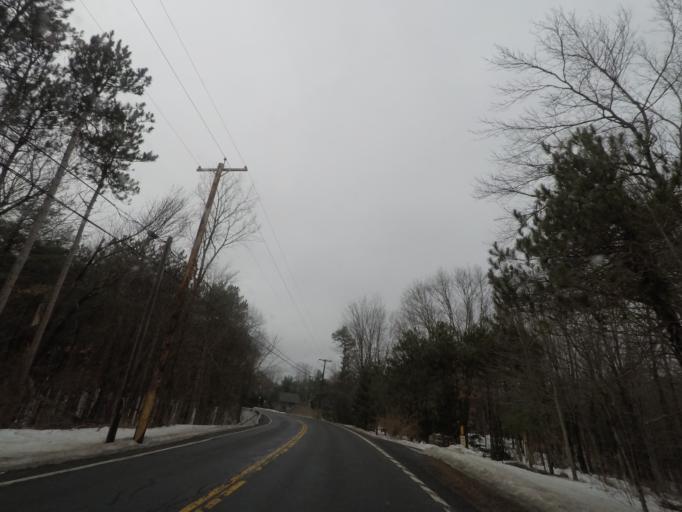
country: US
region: New York
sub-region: Albany County
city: Voorheesville
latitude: 42.6586
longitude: -73.9820
